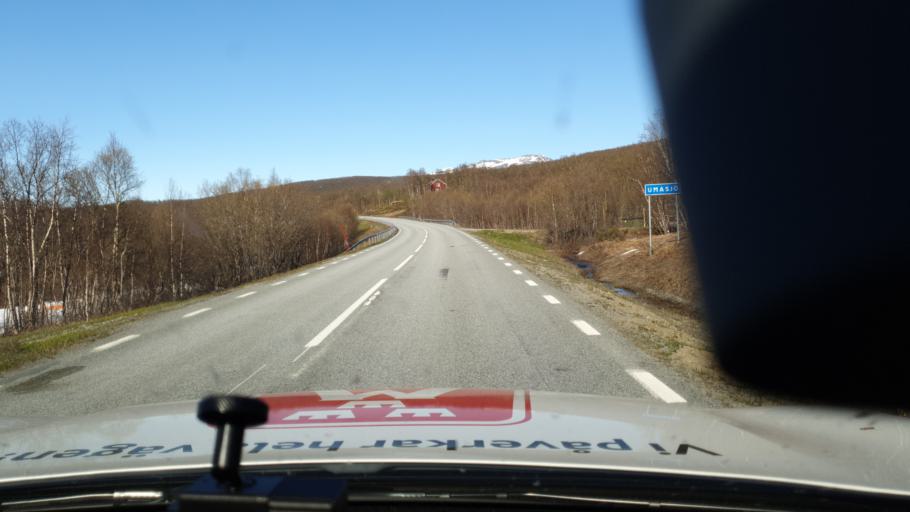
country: NO
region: Nordland
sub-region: Rana
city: Mo i Rana
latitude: 65.9717
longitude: 15.0570
